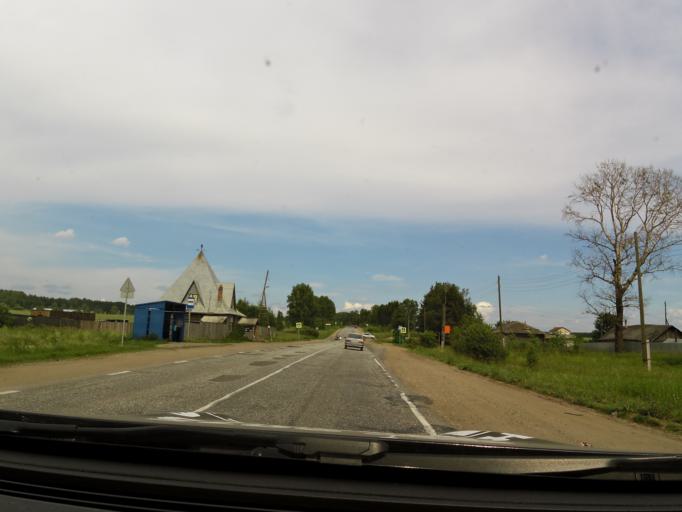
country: RU
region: Kirov
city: Vakhrushi
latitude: 58.6393
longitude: 49.8447
